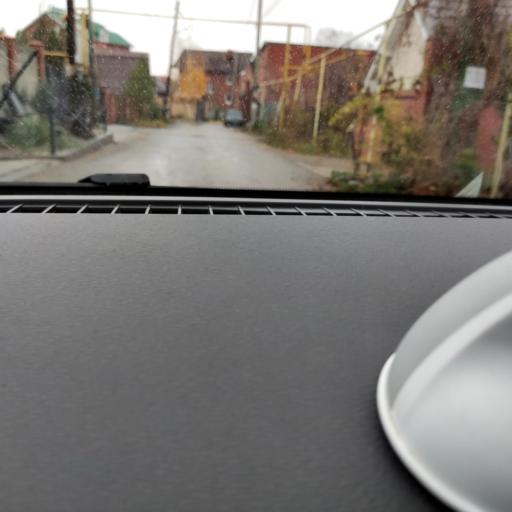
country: RU
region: Samara
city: Samara
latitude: 53.2700
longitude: 50.2066
